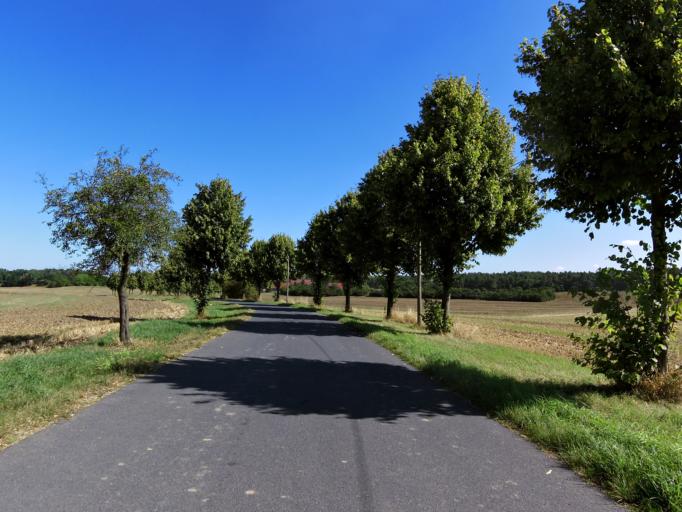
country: DE
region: Saxony
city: Strehla
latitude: 51.3785
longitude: 13.2596
